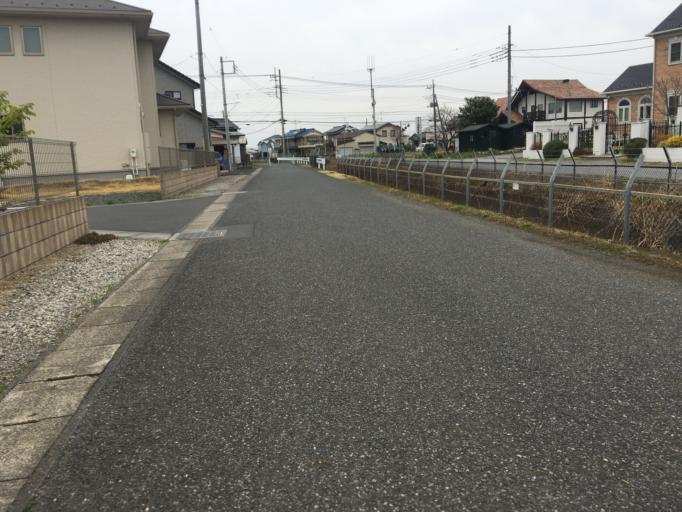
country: JP
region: Saitama
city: Kazo
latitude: 36.1107
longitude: 139.5920
